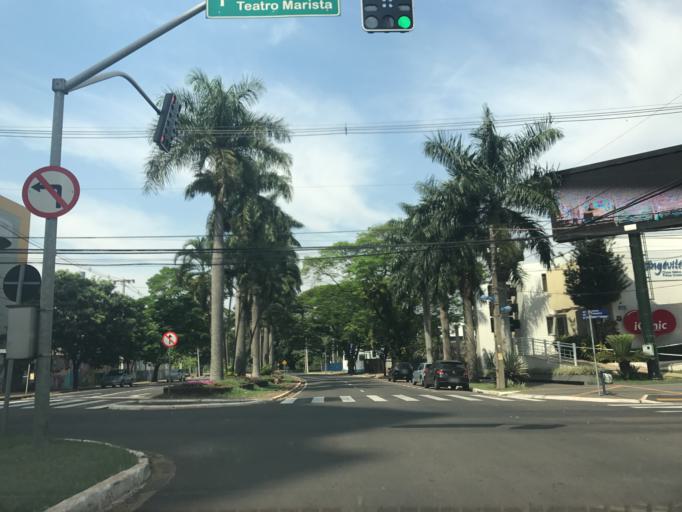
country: BR
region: Parana
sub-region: Maringa
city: Maringa
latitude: -23.4254
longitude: -51.9434
